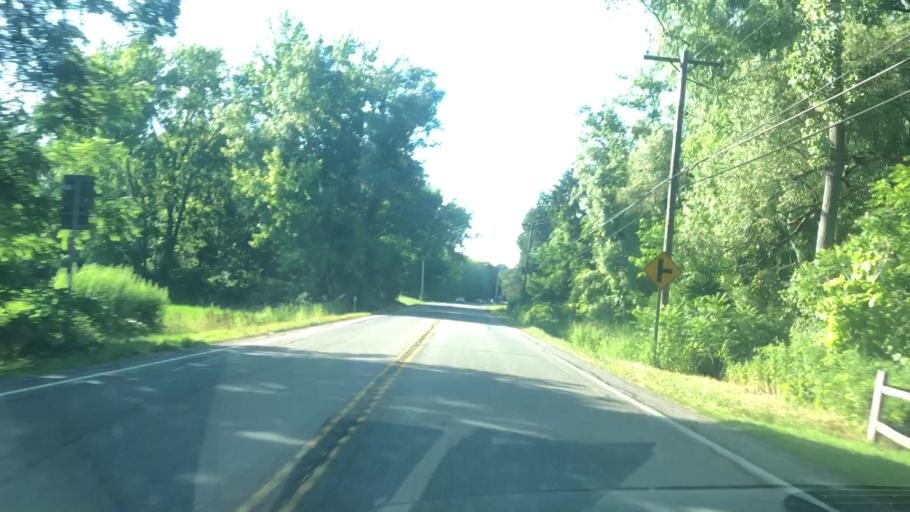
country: US
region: New York
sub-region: Wayne County
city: Ontario
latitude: 43.1847
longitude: -77.2895
